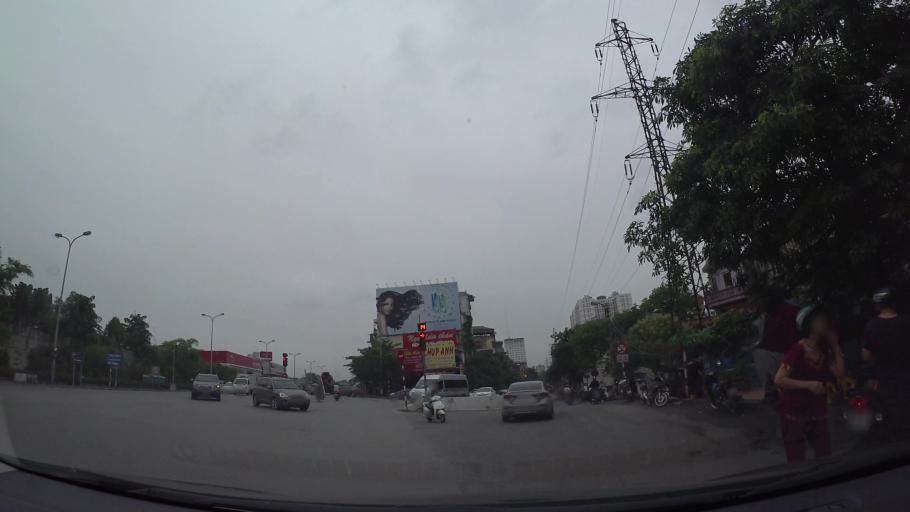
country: VN
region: Ha Noi
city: Hai BaTrung
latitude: 21.0056
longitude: 105.8687
